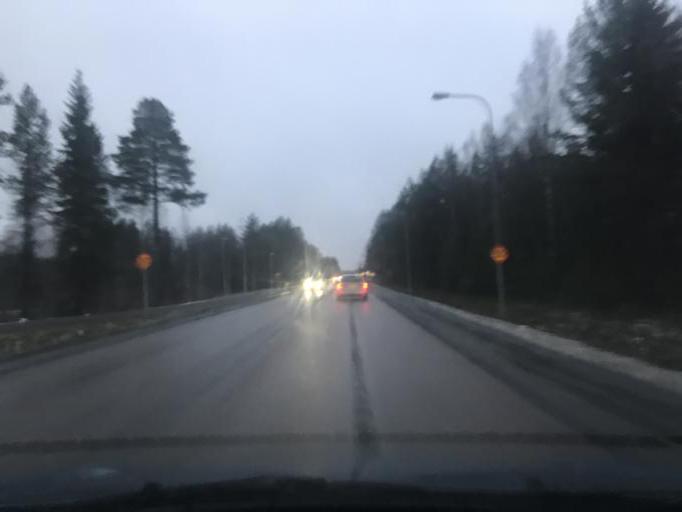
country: SE
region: Norrbotten
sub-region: Lulea Kommun
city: Gammelstad
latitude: 65.6283
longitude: 22.0371
